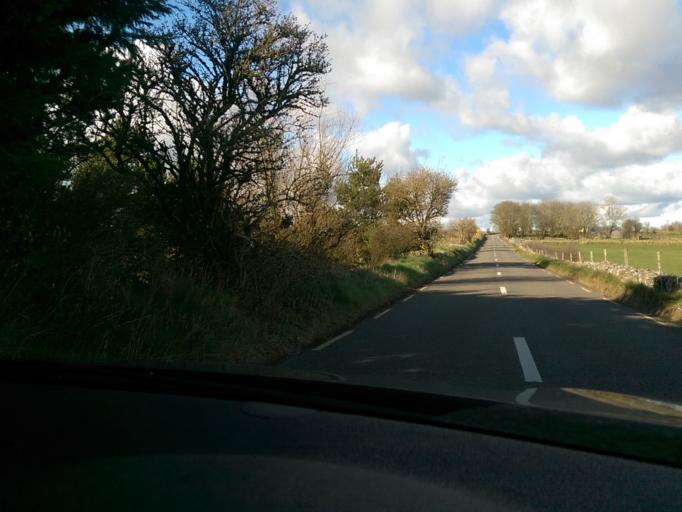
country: IE
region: Connaught
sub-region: Roscommon
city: Castlerea
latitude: 53.5712
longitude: -8.5673
